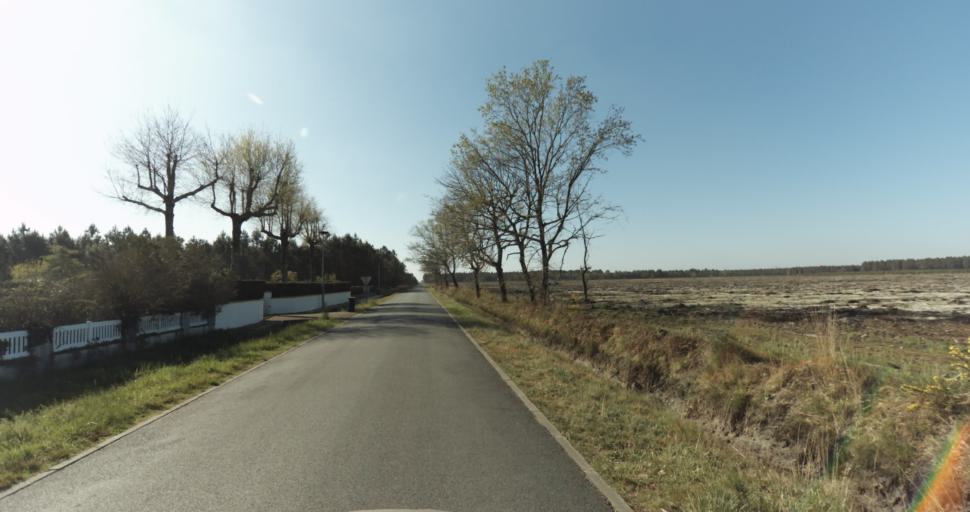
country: FR
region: Aquitaine
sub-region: Departement de la Gironde
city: Martignas-sur-Jalle
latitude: 44.7931
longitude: -0.8650
